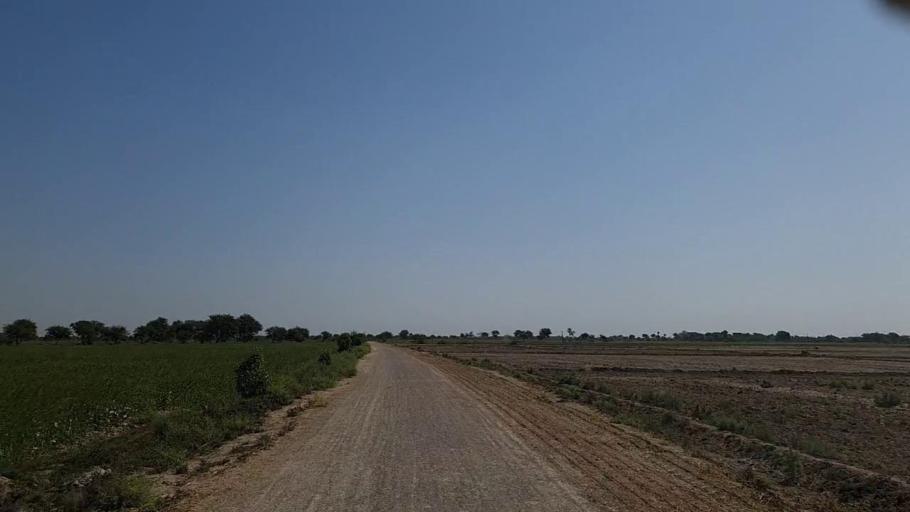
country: PK
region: Sindh
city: Mirpur Batoro
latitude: 24.6815
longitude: 68.2892
